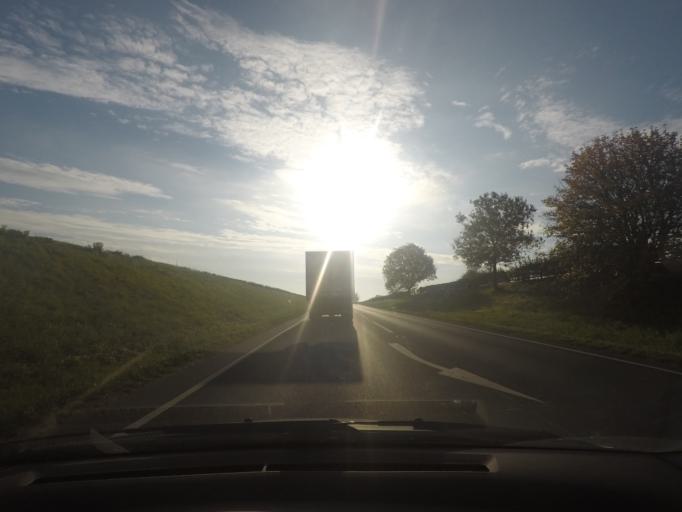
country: GB
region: England
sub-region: East Riding of Yorkshire
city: Hayton
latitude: 53.8843
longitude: -0.7236
